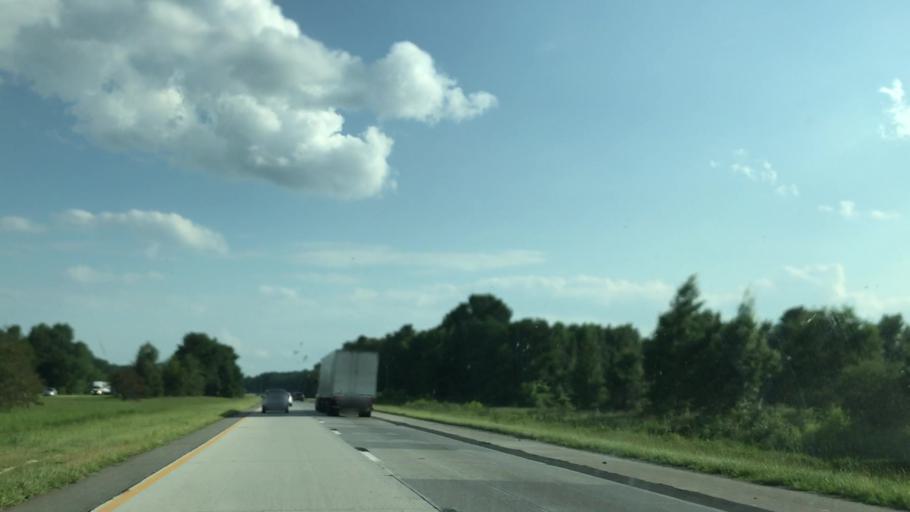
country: US
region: South Carolina
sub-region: Dorchester County
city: Saint George
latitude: 33.1677
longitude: -80.6184
